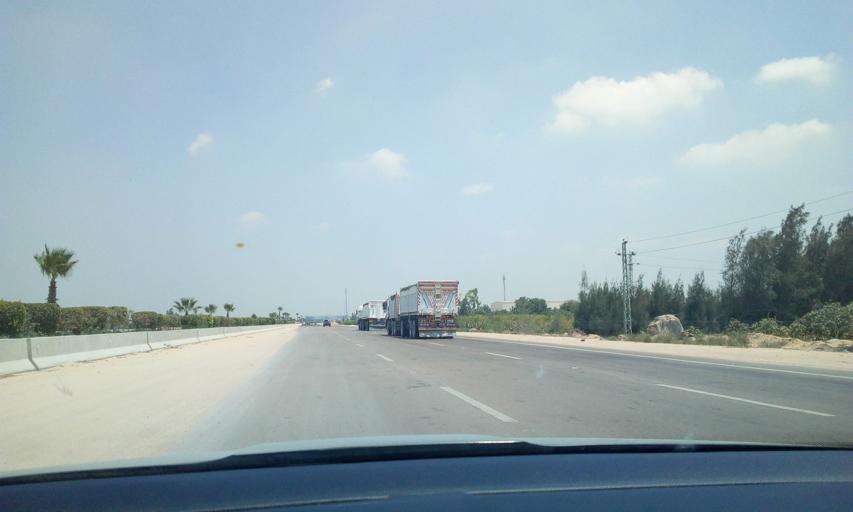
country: EG
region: Al Buhayrah
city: Beheira
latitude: 30.5019
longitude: 30.2118
